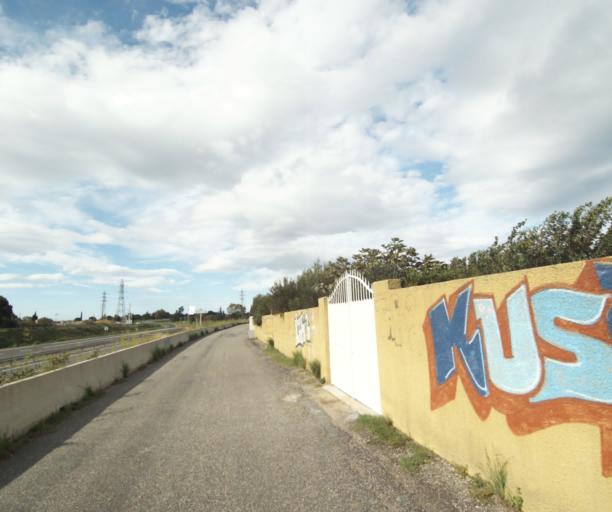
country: FR
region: Languedoc-Roussillon
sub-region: Departement des Pyrenees-Orientales
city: Argelers
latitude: 42.5474
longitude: 3.0072
